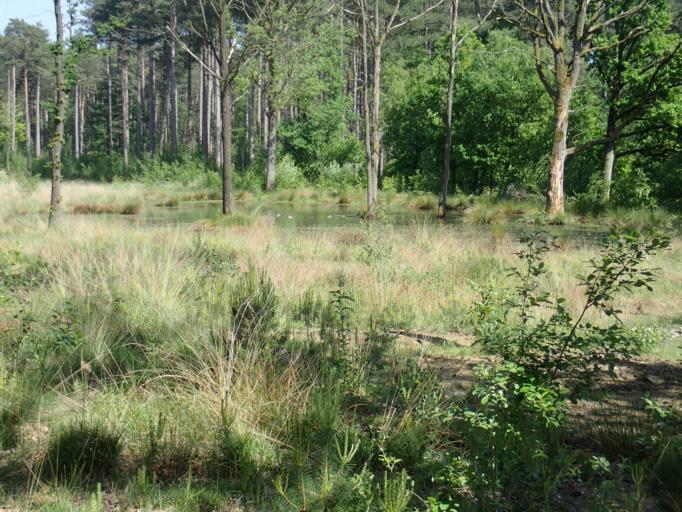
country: BE
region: Flanders
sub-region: Provincie Antwerpen
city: Westerlo
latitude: 51.0608
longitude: 4.9123
